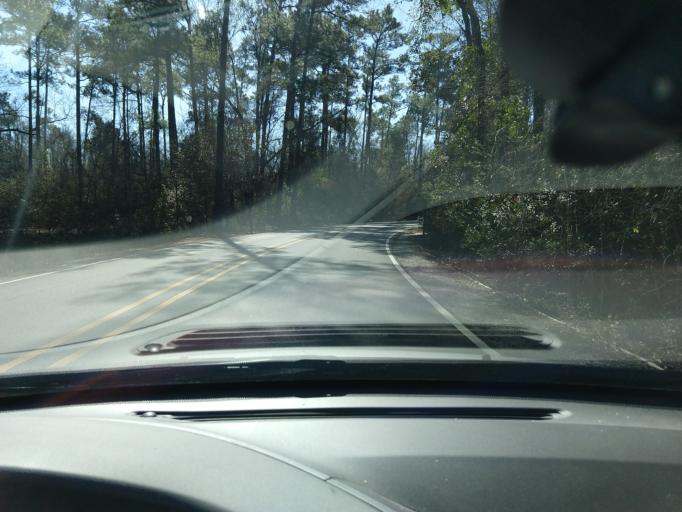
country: US
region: Mississippi
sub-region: Jackson County
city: Gulf Park Estates
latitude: 30.3925
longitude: -88.7881
